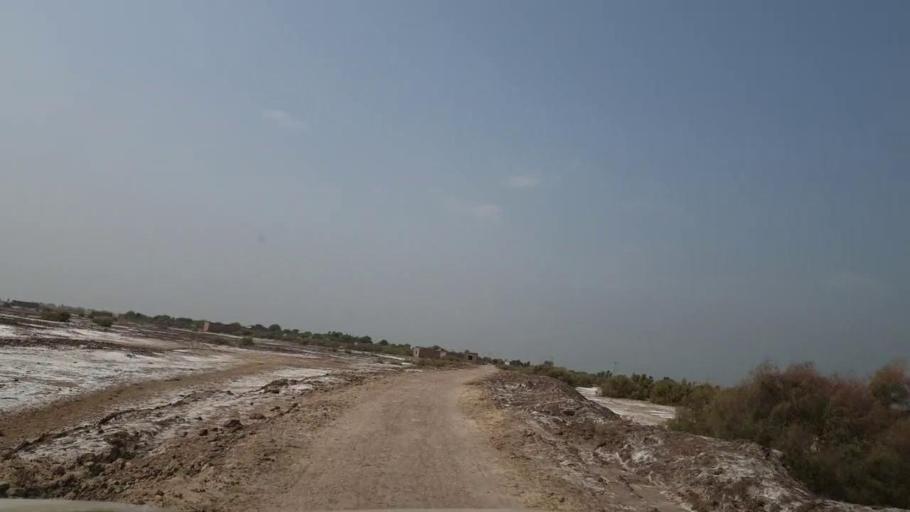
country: PK
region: Sindh
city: Dokri
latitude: 27.4196
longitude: 68.2056
